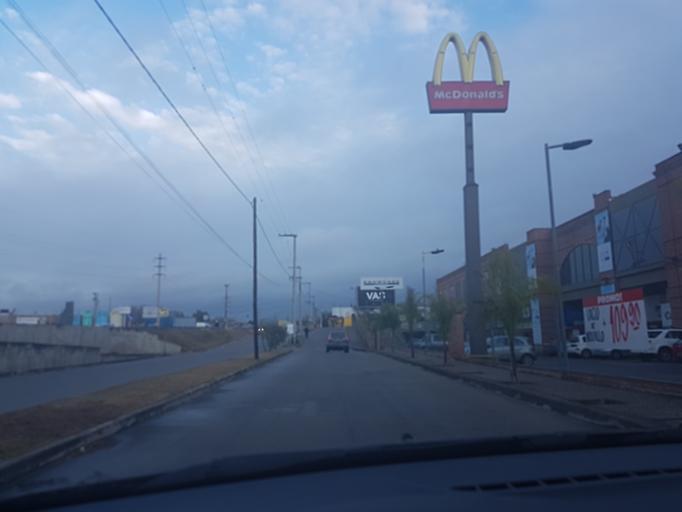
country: AR
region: Cordoba
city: Villa Allende
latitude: -31.3004
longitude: -64.2765
